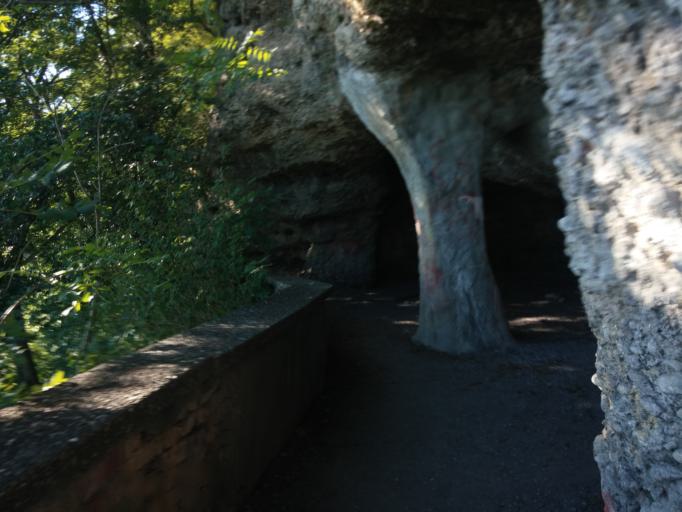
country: DE
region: Baden-Wuerttemberg
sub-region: Tuebingen Region
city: Heiligenberg
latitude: 47.8233
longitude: 9.3056
